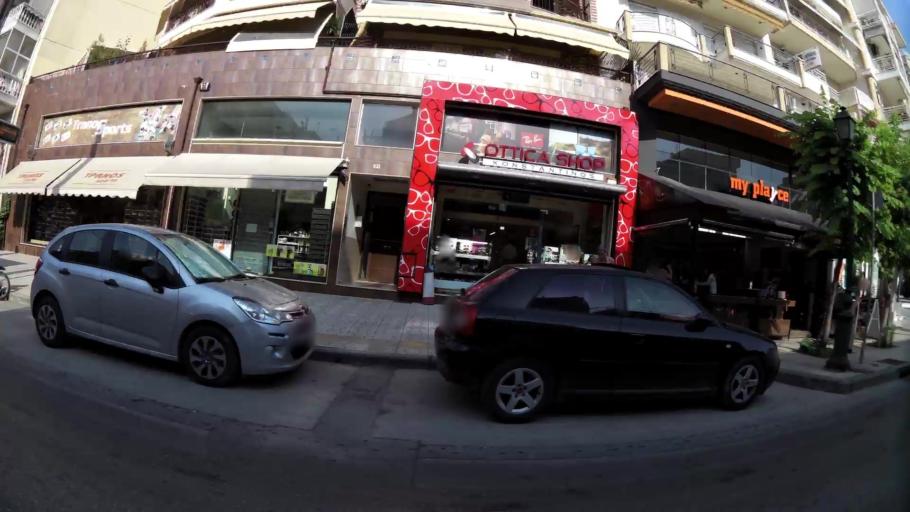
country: GR
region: Central Macedonia
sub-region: Nomos Thessalonikis
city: Evosmos
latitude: 40.6661
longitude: 22.9118
